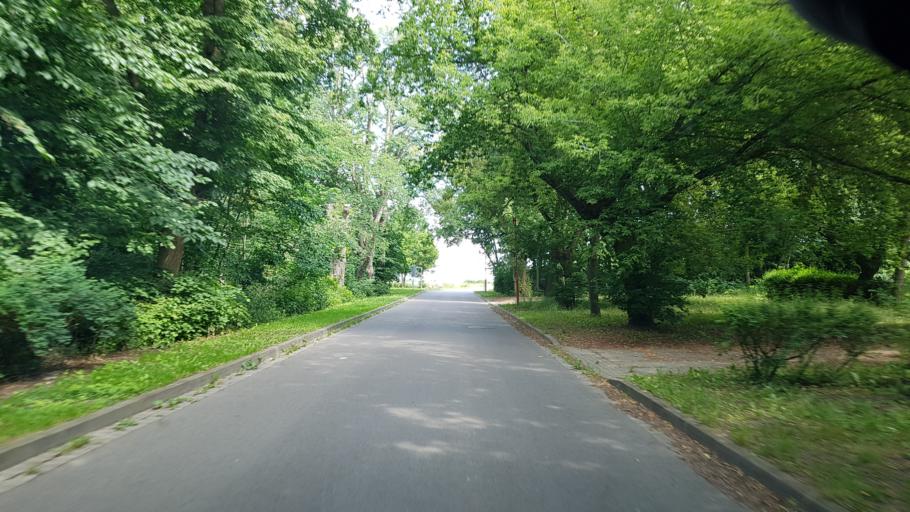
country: DE
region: Brandenburg
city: Prenzlau
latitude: 53.3632
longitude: 13.8037
